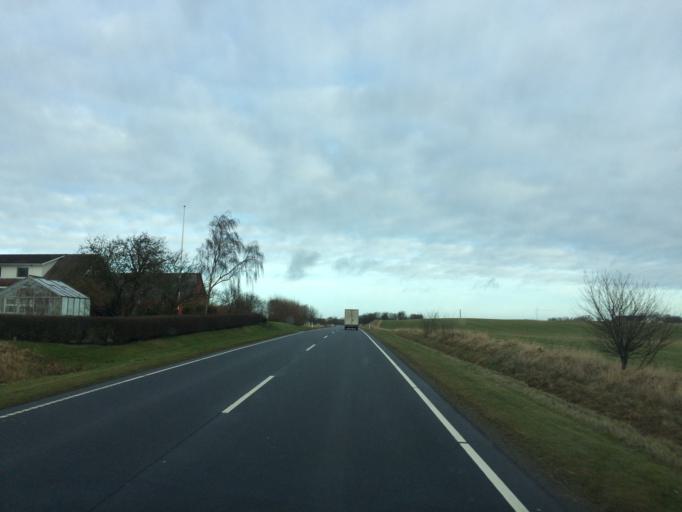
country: DK
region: Central Jutland
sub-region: Struer Kommune
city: Struer
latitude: 56.4602
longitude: 8.5437
